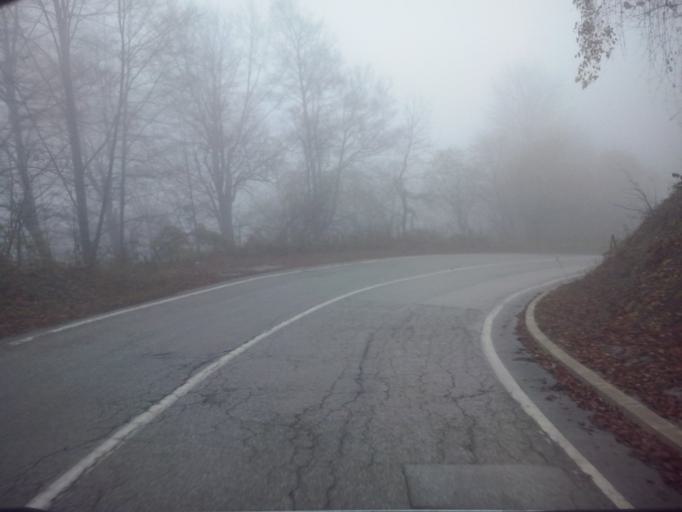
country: RS
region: Central Serbia
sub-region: Moravicki Okrug
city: Ivanjica
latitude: 43.5307
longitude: 20.3105
